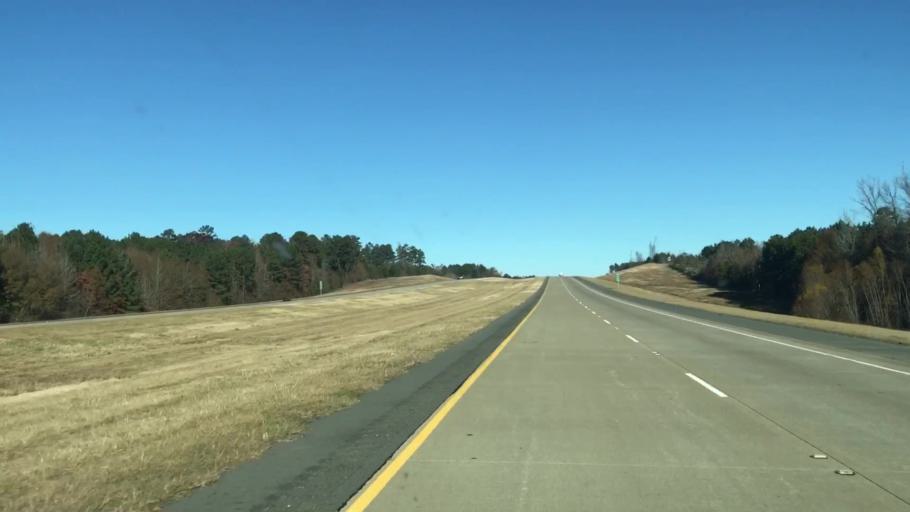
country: US
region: Louisiana
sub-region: Caddo Parish
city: Vivian
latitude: 32.9662
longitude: -93.9052
